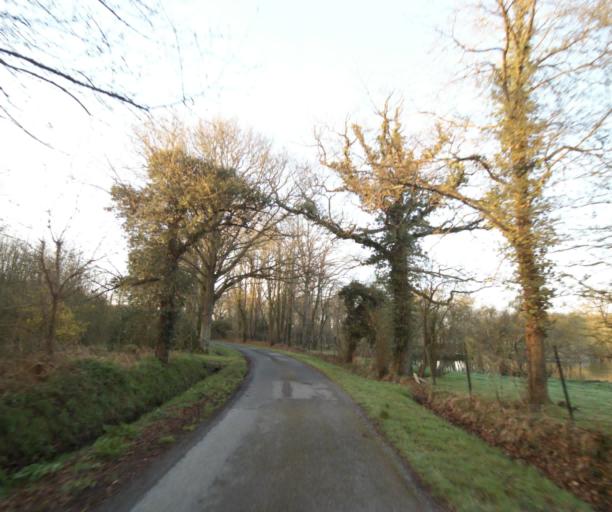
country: FR
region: Pays de la Loire
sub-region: Departement de la Loire-Atlantique
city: Bouvron
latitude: 47.4315
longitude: -1.8853
